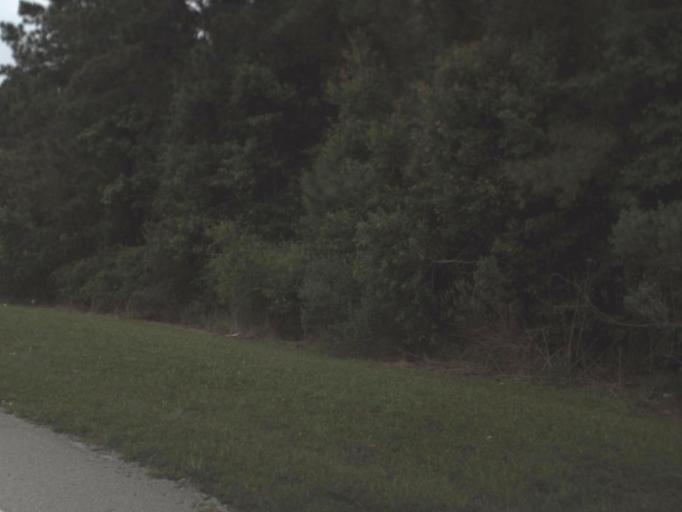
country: US
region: Florida
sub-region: Clay County
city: Orange Park
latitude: 30.2072
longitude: -81.7063
